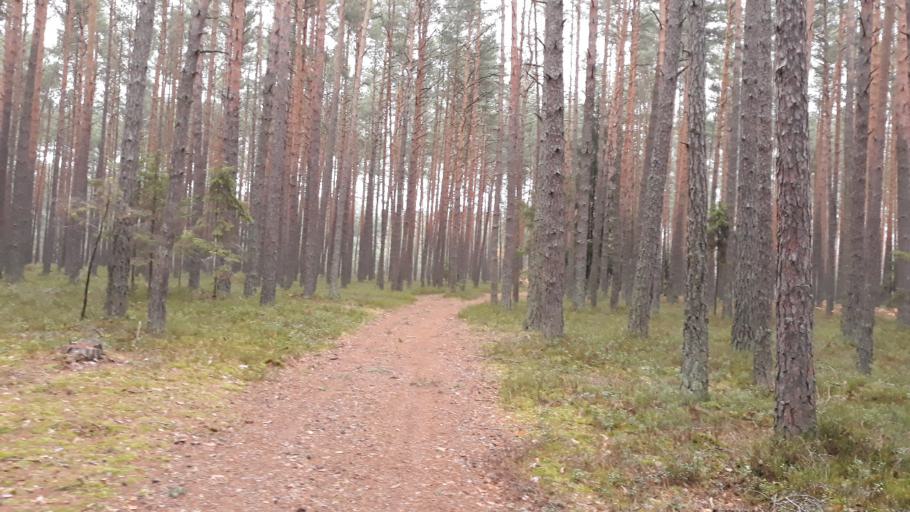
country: PL
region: Lublin Voivodeship
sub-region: Powiat janowski
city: Dzwola
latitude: 50.6523
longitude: 22.5751
